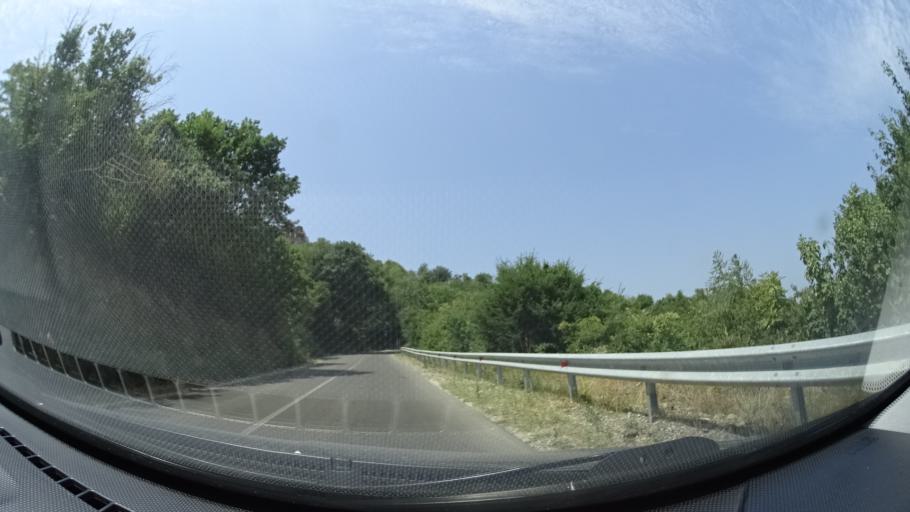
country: GE
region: Kakheti
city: Sighnaghi
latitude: 41.6218
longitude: 45.9305
